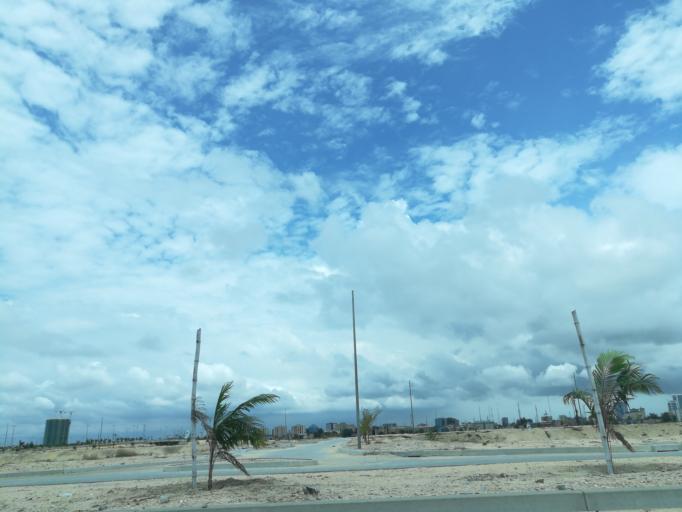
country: NG
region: Lagos
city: Ikoyi
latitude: 6.4106
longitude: 3.4214
